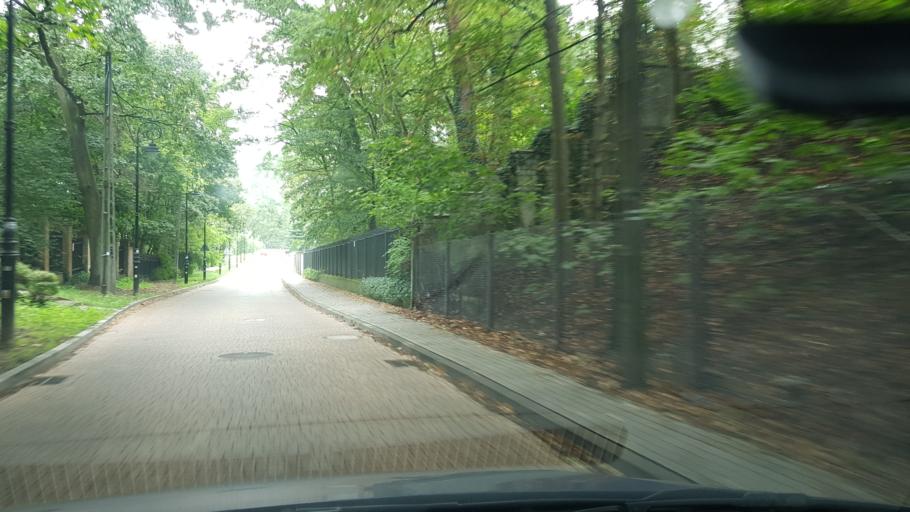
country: PL
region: Masovian Voivodeship
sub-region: Powiat piaseczynski
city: Konstancin-Jeziorna
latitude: 52.1017
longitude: 21.1104
